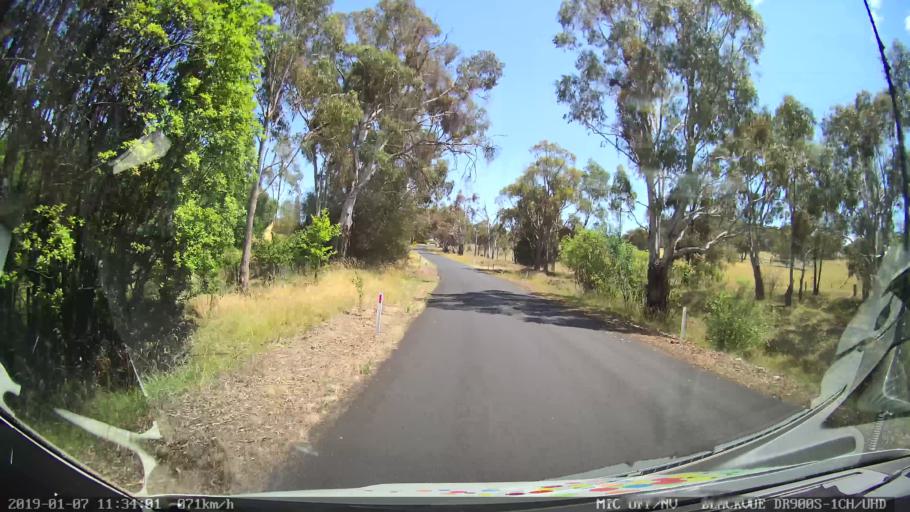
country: AU
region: New South Wales
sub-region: Armidale Dumaresq
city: Armidale
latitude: -30.3939
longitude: 151.5604
